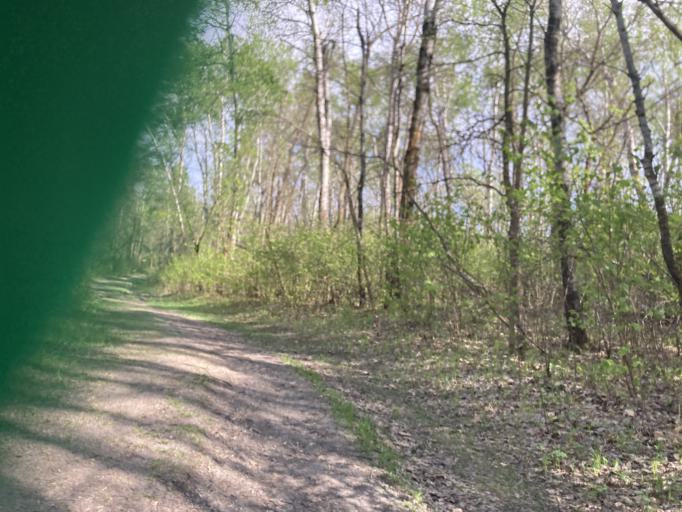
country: CA
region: Manitoba
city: Brandon
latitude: 49.7213
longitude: -99.9077
